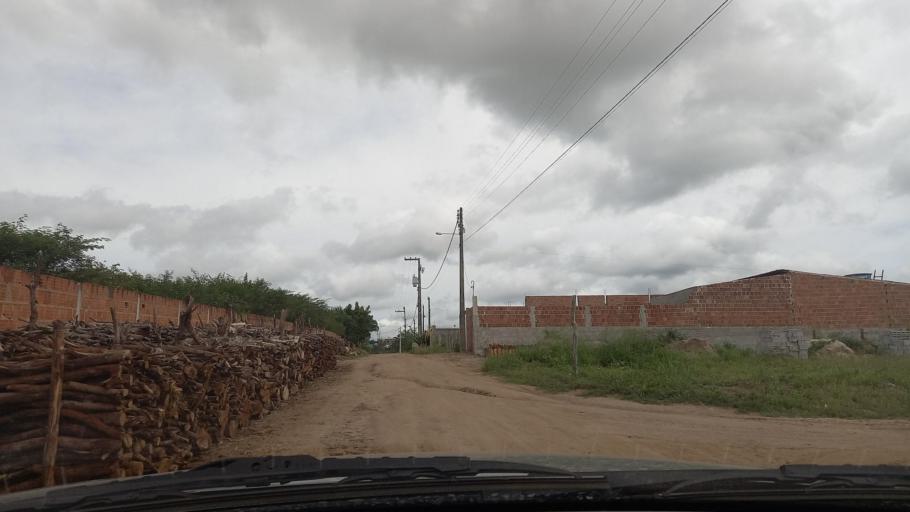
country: BR
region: Pernambuco
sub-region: Gravata
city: Gravata
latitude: -8.1899
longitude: -35.5826
